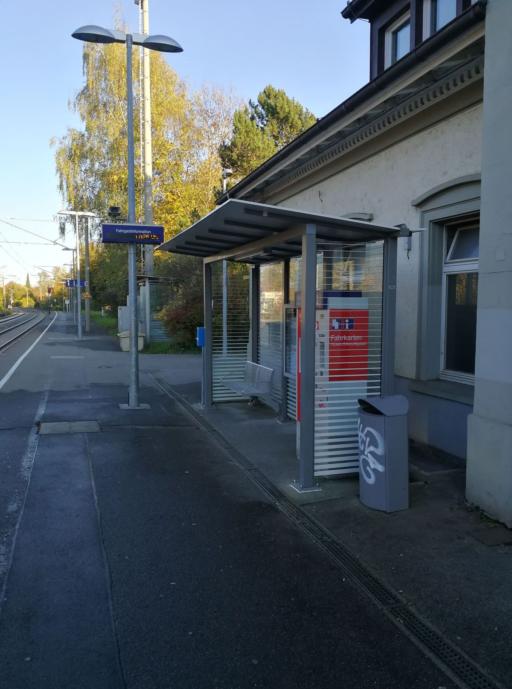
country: DE
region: Baden-Wuerttemberg
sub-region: Freiburg Region
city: Gottmadingen
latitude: 47.7373
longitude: 8.7753
